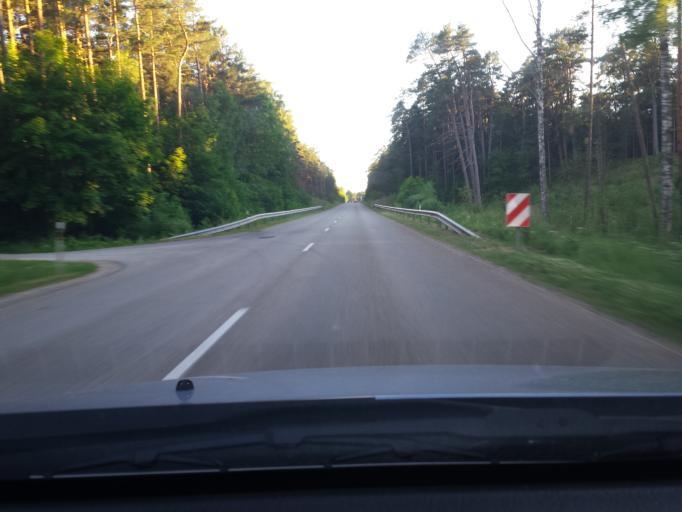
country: LV
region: Riga
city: Jaunciems
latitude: 57.0880
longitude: 24.1728
